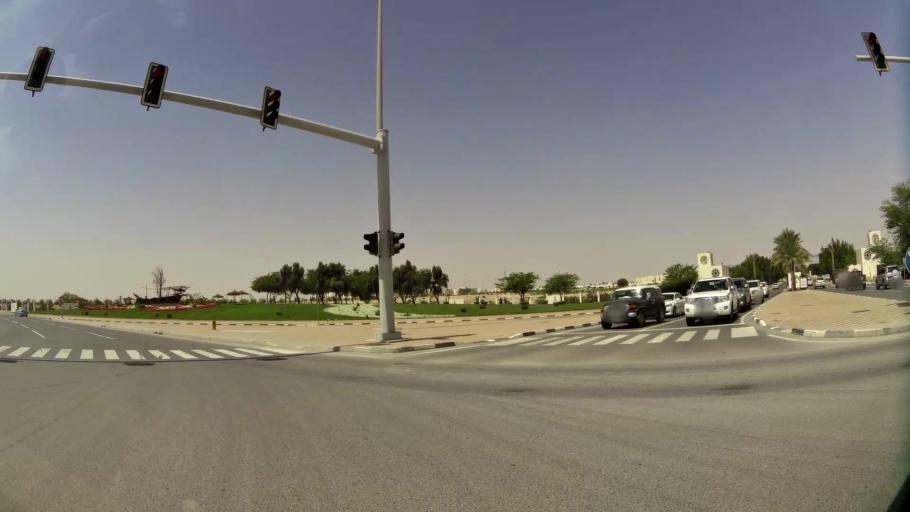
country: QA
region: Baladiyat ad Dawhah
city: Doha
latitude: 25.3660
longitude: 51.4961
